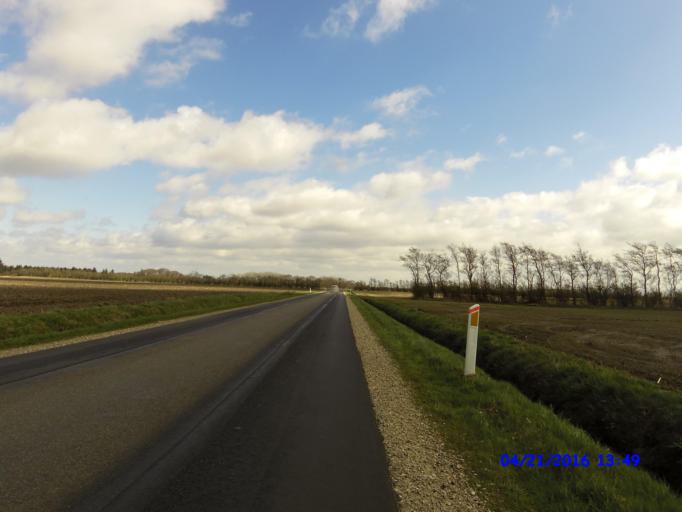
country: DK
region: South Denmark
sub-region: Haderslev Kommune
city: Gram
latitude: 55.2452
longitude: 8.9847
